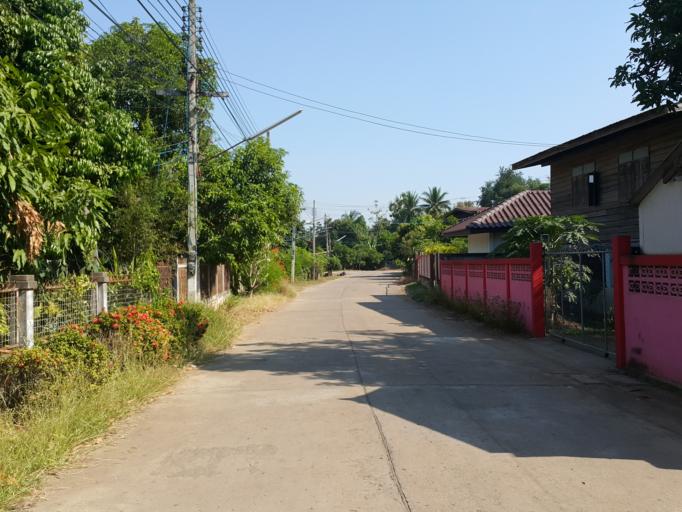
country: TH
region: Sukhothai
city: Thung Saliam
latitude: 17.3171
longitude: 99.5561
